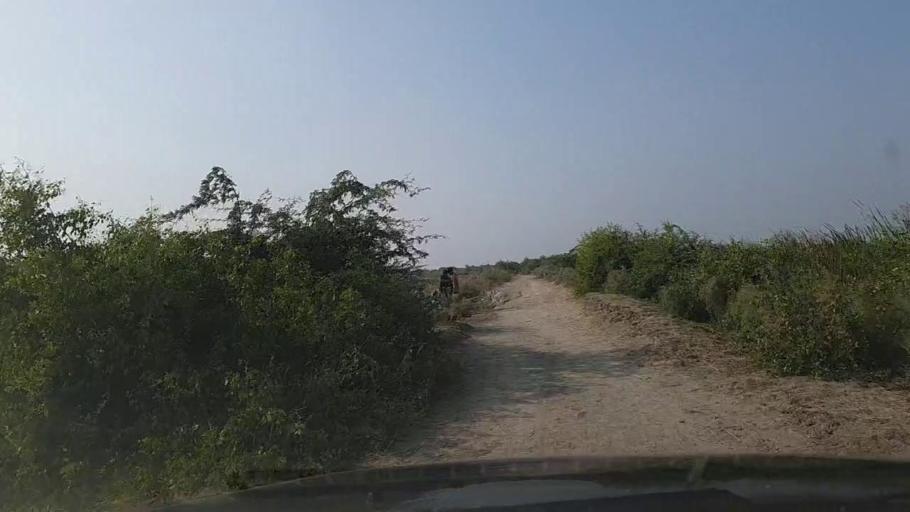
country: PK
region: Sindh
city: Mirpur Batoro
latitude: 24.6457
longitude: 68.2813
